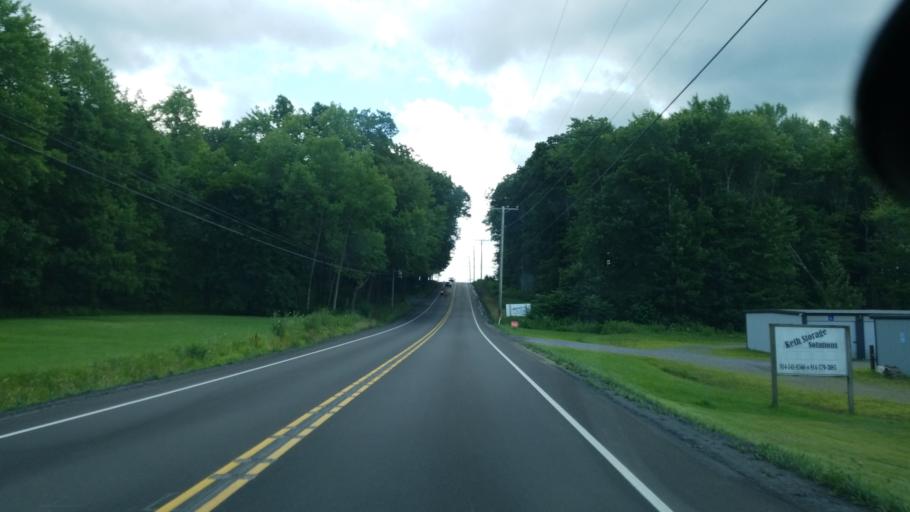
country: US
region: Pennsylvania
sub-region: Jefferson County
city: Brookville
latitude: 41.2657
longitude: -79.1082
